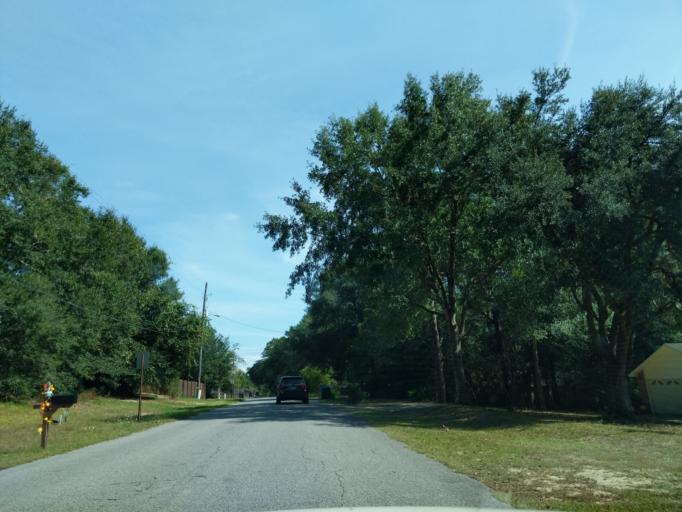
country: US
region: Florida
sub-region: Okaloosa County
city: Crestview
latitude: 30.7048
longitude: -86.5863
